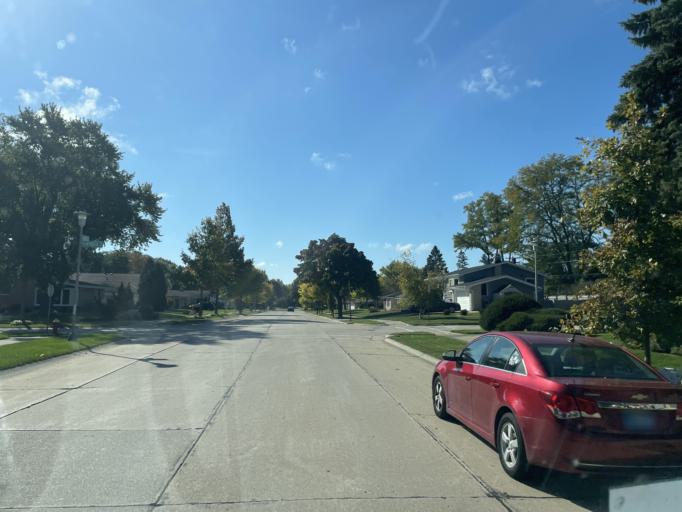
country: US
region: Wisconsin
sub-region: Milwaukee County
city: Oak Creek
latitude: 42.8999
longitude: -87.9068
